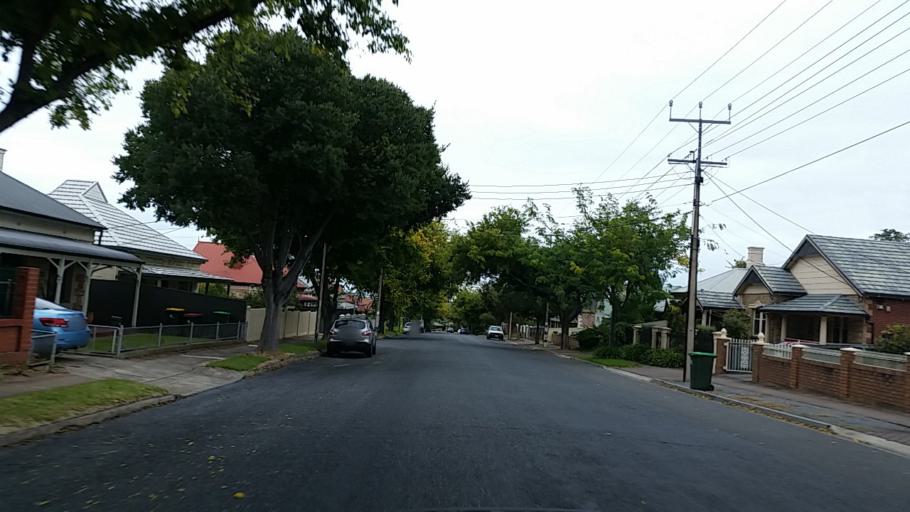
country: AU
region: South Australia
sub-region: Prospect
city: Prospect
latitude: -34.8799
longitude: 138.5965
